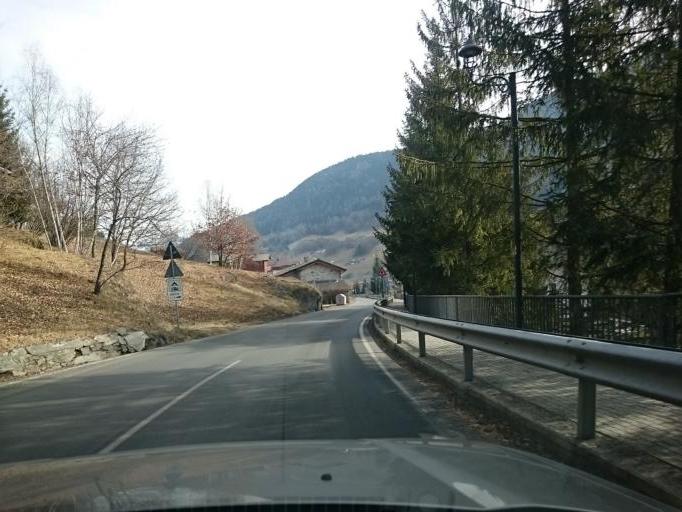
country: IT
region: Lombardy
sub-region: Provincia di Sondrio
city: Aprica
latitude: 46.1581
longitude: 10.1735
